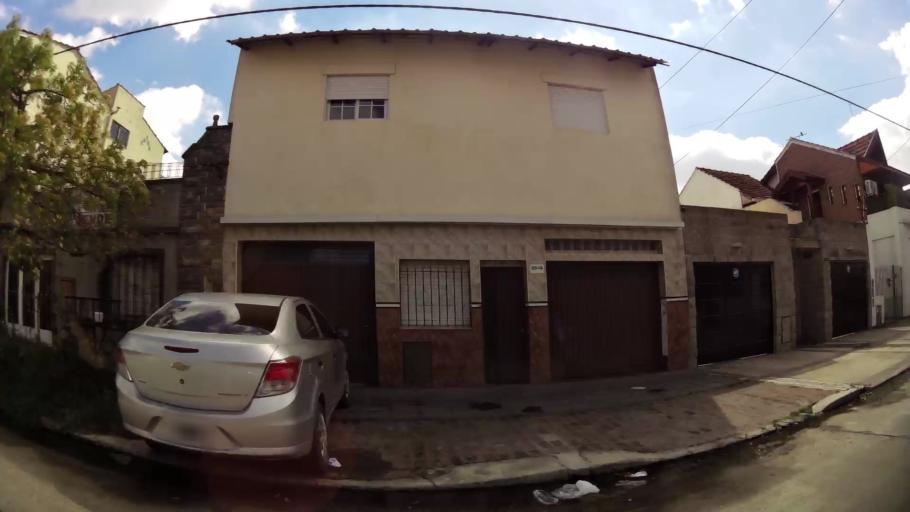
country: AR
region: Buenos Aires
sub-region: Partido de Lanus
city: Lanus
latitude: -34.6788
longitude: -58.4105
